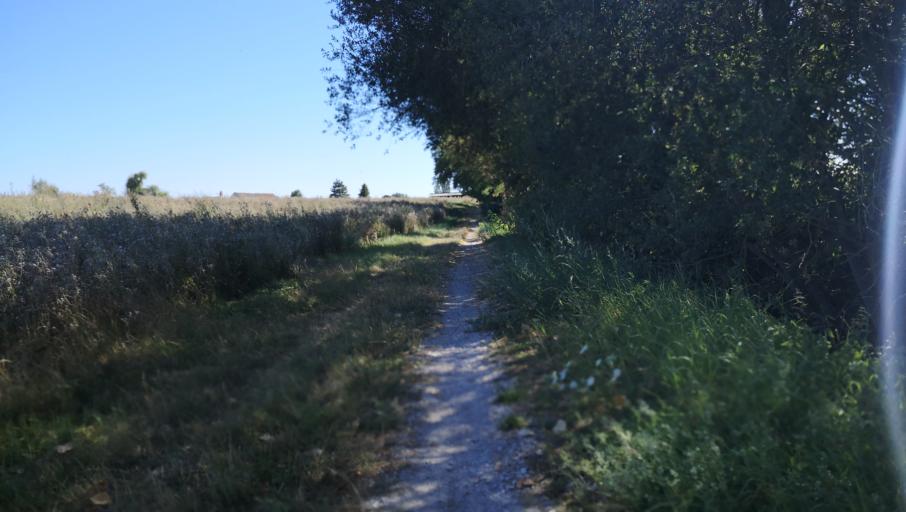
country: FR
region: Centre
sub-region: Departement du Loiret
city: Semoy
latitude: 47.9382
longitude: 1.9609
